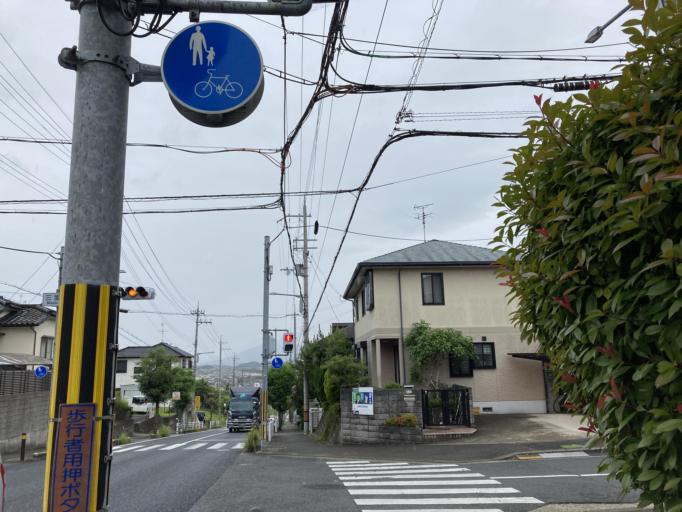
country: JP
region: Nara
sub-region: Ikoma-shi
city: Ikoma
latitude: 34.6346
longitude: 135.7065
